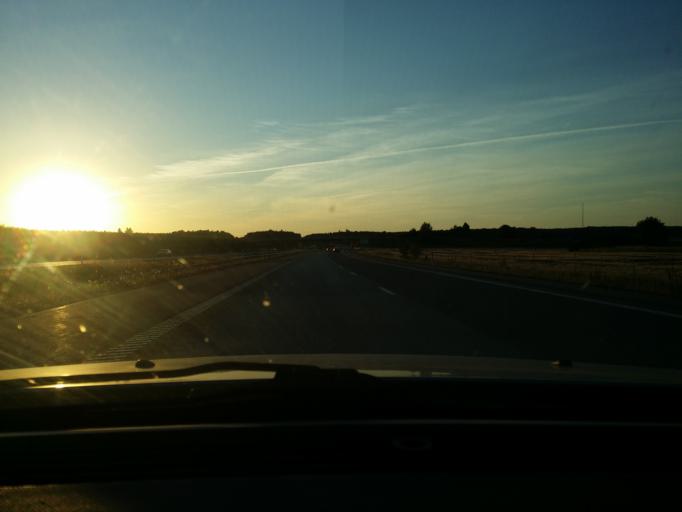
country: SE
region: Uppsala
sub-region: Habo Kommun
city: Balsta
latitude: 59.6009
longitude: 17.4400
